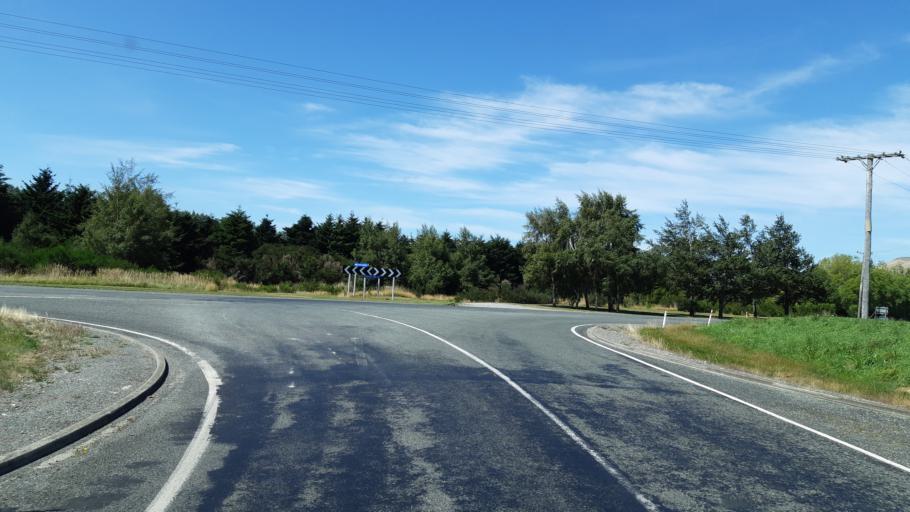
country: NZ
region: Southland
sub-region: Gore District
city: Gore
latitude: -45.9823
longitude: 168.7982
